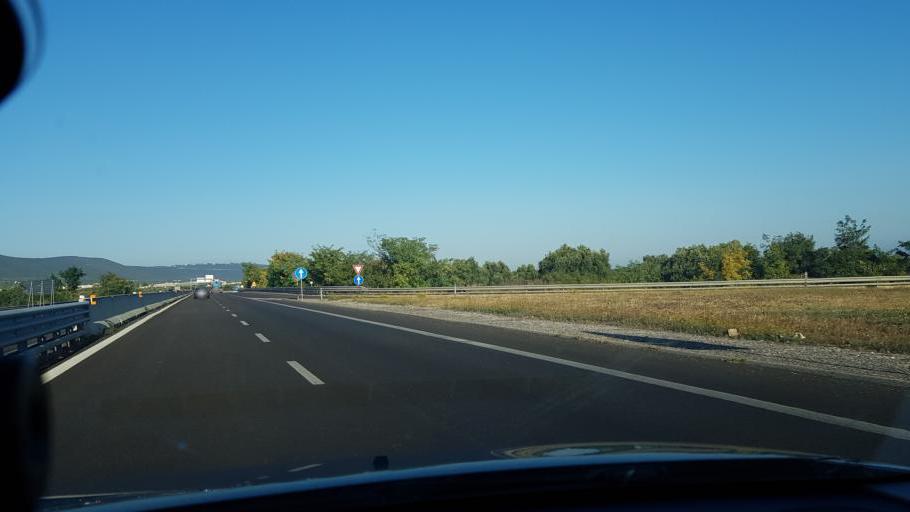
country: IT
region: Apulia
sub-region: Provincia di Brindisi
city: Fasano
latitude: 40.8407
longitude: 17.3718
